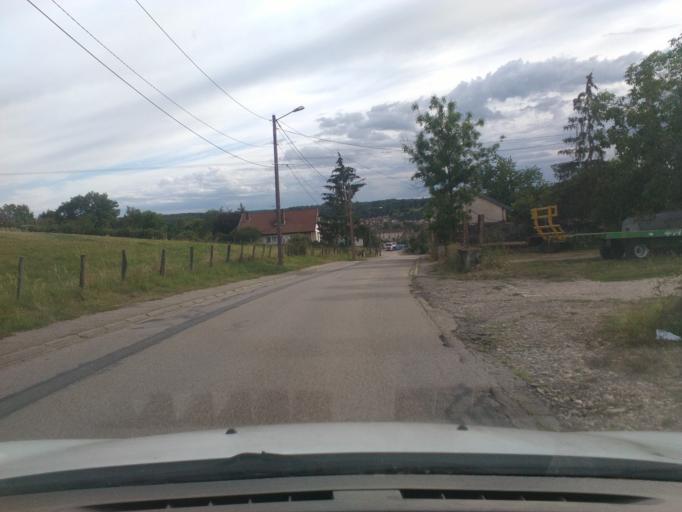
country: FR
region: Lorraine
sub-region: Departement des Vosges
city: Chatel-sur-Moselle
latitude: 48.3158
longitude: 6.3976
